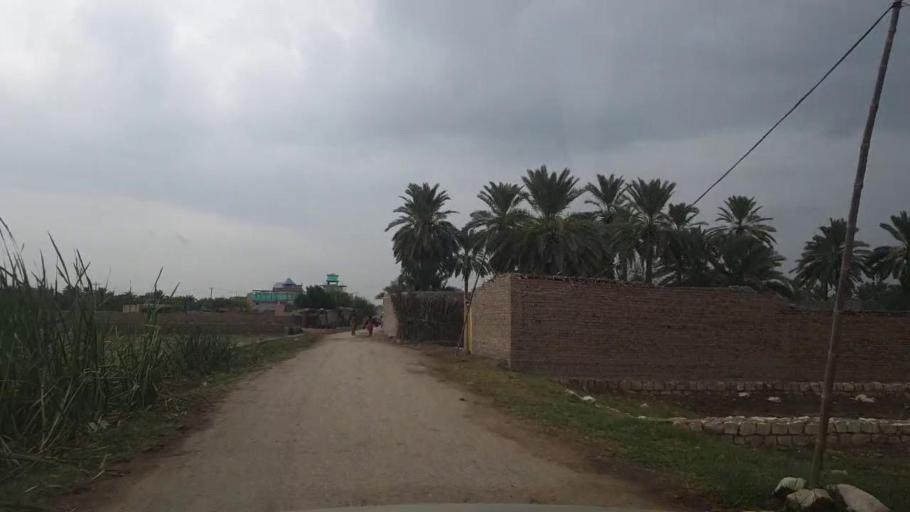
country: PK
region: Sindh
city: Khairpur
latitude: 27.5413
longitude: 68.7367
